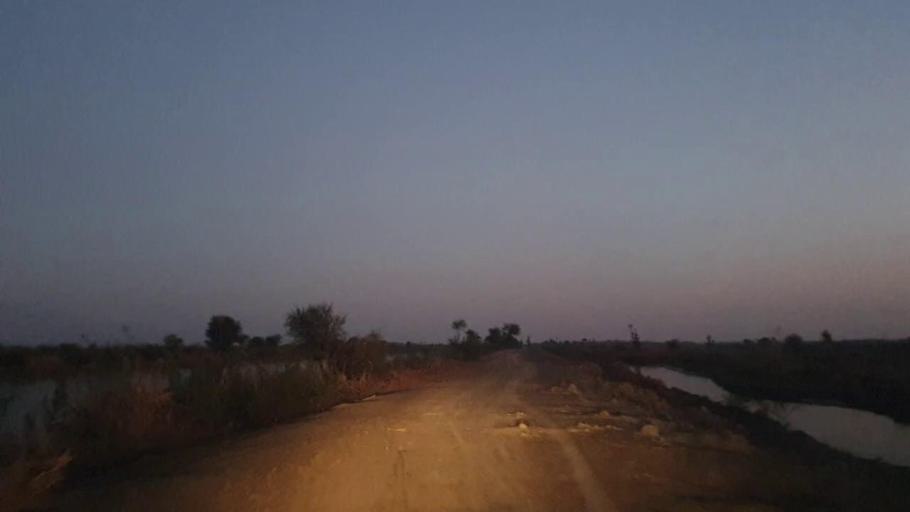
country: PK
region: Sindh
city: Tando Mittha Khan
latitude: 26.0483
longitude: 69.1741
